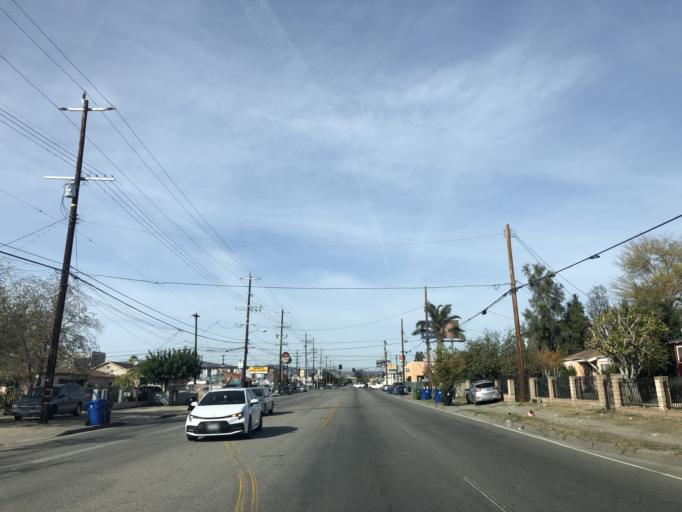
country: US
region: California
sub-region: Los Angeles County
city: San Fernando
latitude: 34.2572
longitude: -118.4305
